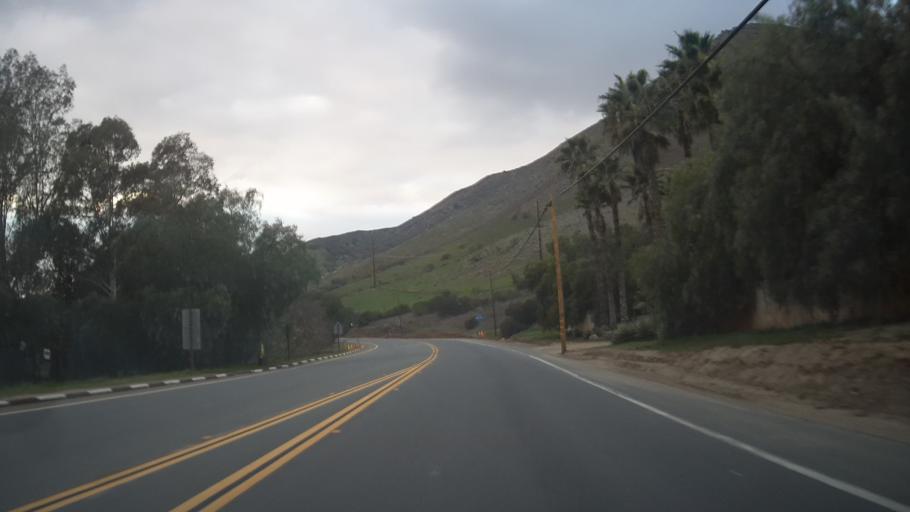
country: US
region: California
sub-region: San Diego County
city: Crest
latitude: 32.7817
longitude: -116.8533
